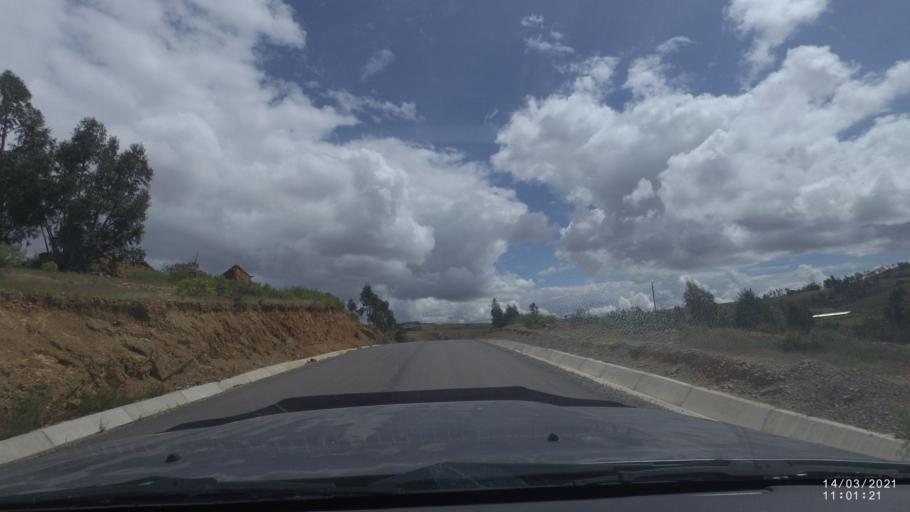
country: BO
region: Cochabamba
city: Tarata
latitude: -17.7955
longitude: -65.9634
